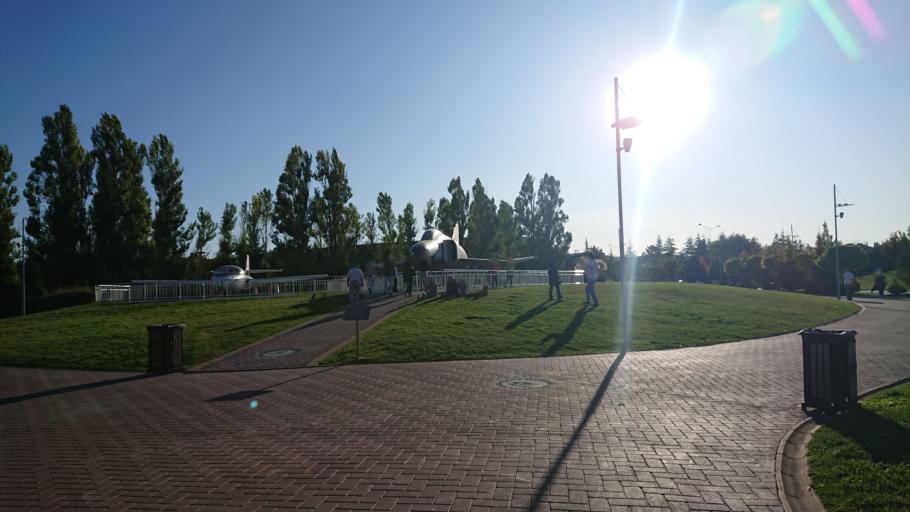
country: TR
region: Eskisehir
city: Eskisehir
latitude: 39.7656
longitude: 30.4729
